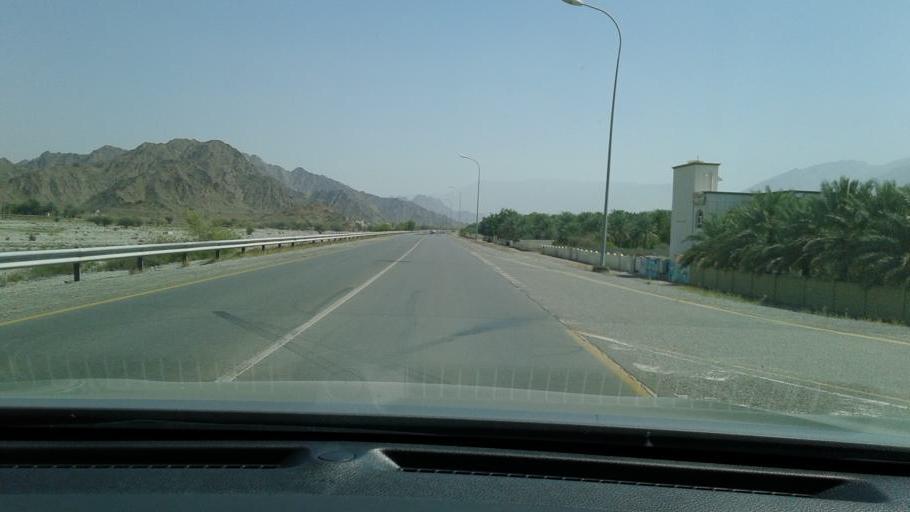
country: OM
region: Al Batinah
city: Rustaq
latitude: 23.3949
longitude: 57.4380
